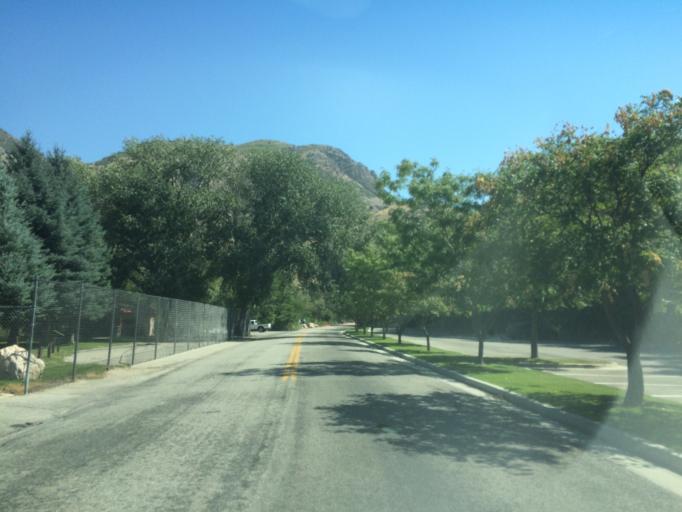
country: US
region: Utah
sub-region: Weber County
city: Ogden
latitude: 41.2378
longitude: -111.9362
